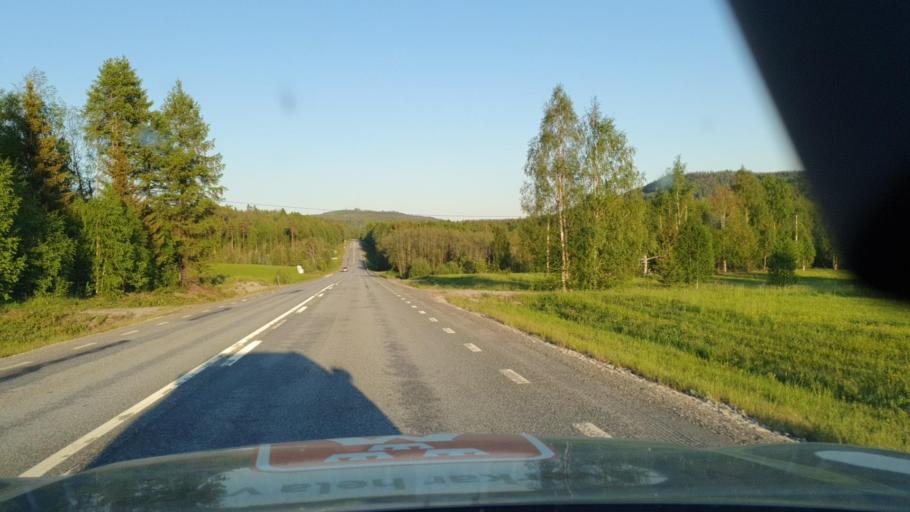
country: SE
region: Vaesternorrland
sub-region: Solleftea Kommun
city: Solleftea
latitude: 63.3203
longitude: 17.1816
